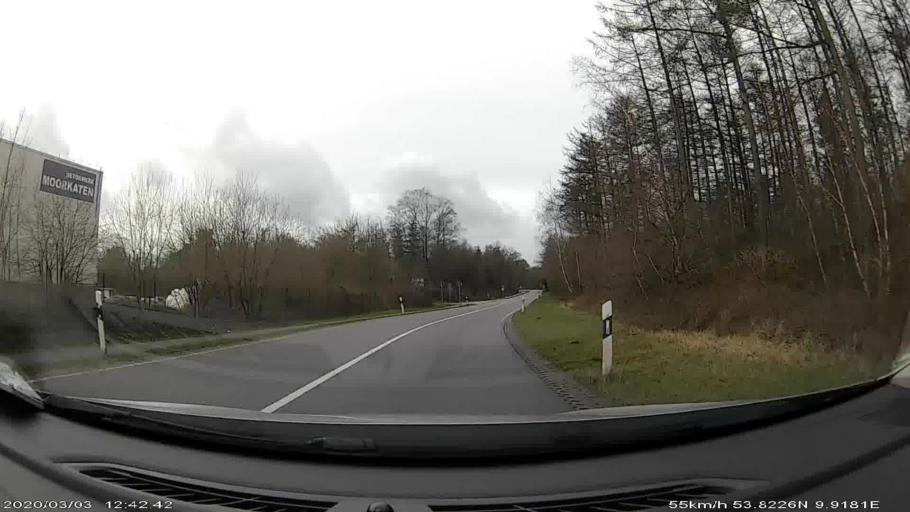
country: DE
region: Schleswig-Holstein
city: Alveslohe
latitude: 53.8226
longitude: 9.9158
